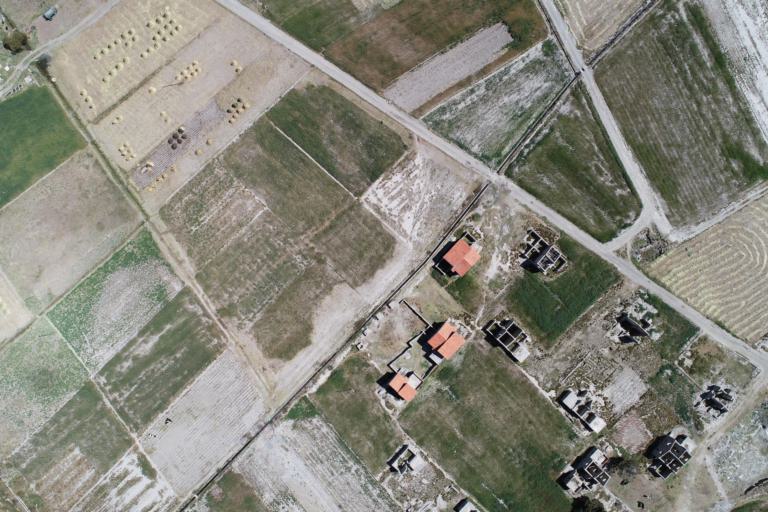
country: BO
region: La Paz
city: Achacachi
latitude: -16.0182
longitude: -68.7177
